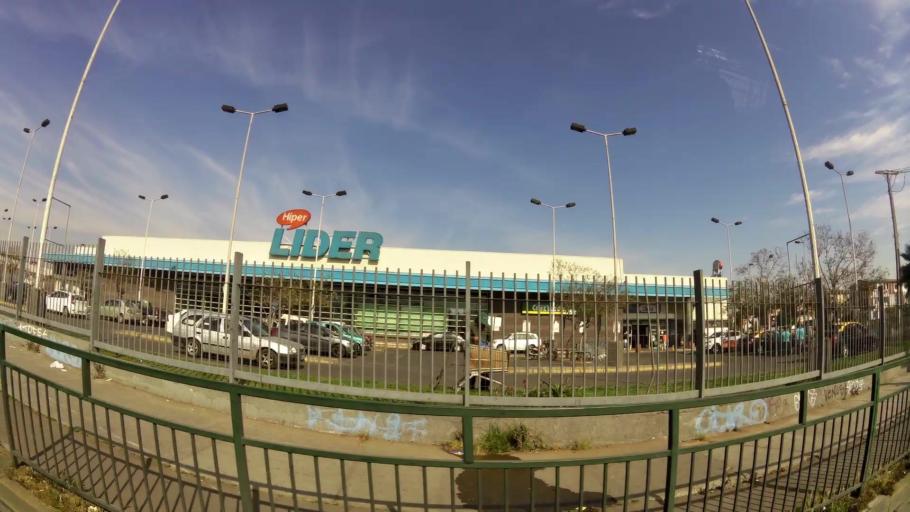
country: CL
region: Santiago Metropolitan
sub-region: Provincia de Santiago
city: La Pintana
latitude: -33.5456
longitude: -70.6338
